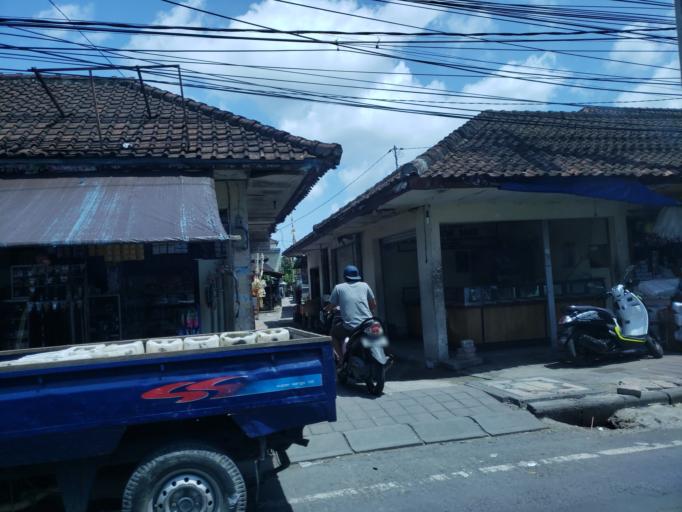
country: ID
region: Bali
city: Kelanabian
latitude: -8.7701
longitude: 115.1734
